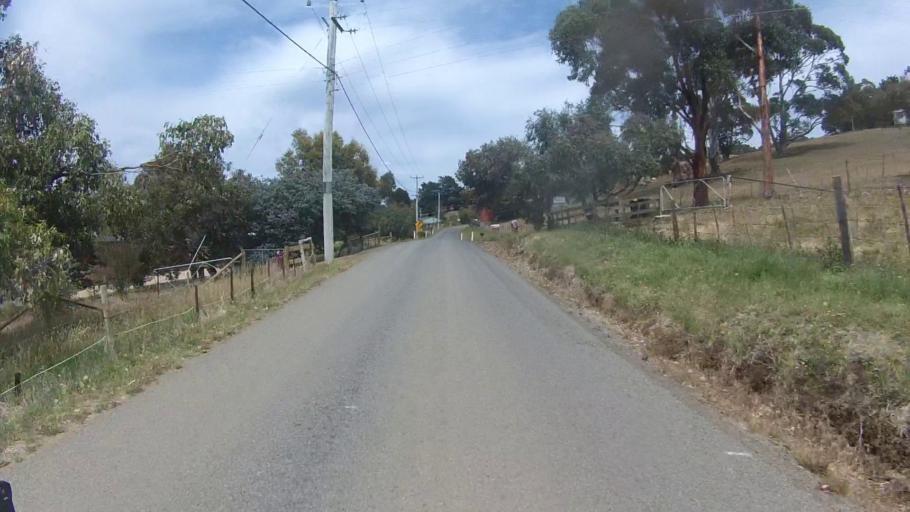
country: AU
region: Tasmania
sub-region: Sorell
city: Sorell
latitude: -42.8065
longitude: 147.8341
